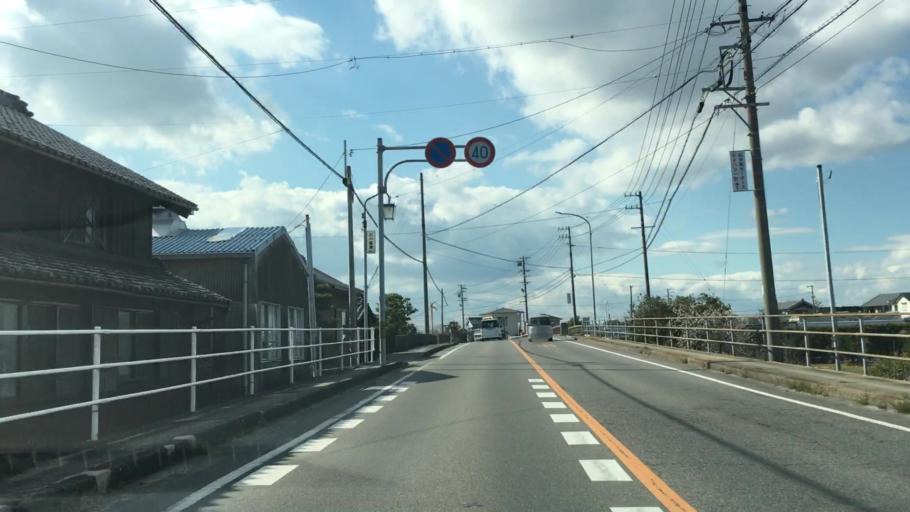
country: JP
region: Aichi
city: Ishiki
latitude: 34.7969
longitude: 137.0555
